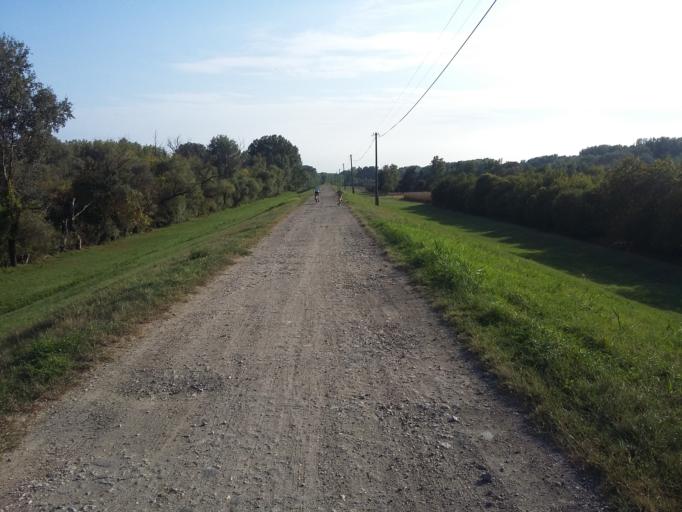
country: HU
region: Csongrad
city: Szeged
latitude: 46.2149
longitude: 20.1205
